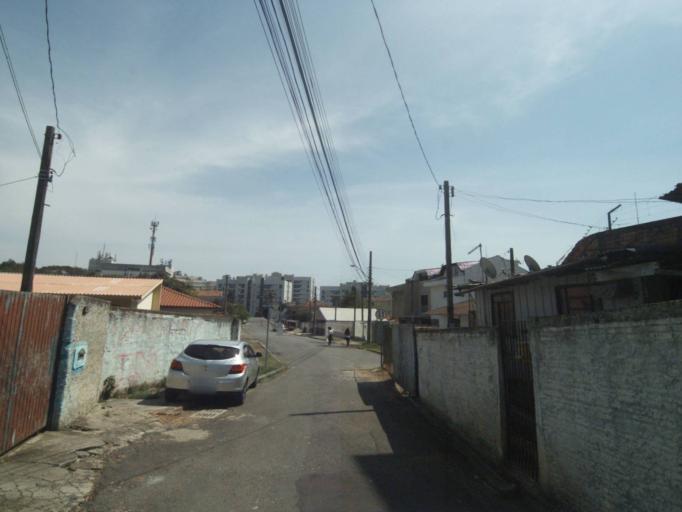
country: BR
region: Parana
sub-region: Curitiba
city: Curitiba
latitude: -25.4698
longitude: -49.2974
